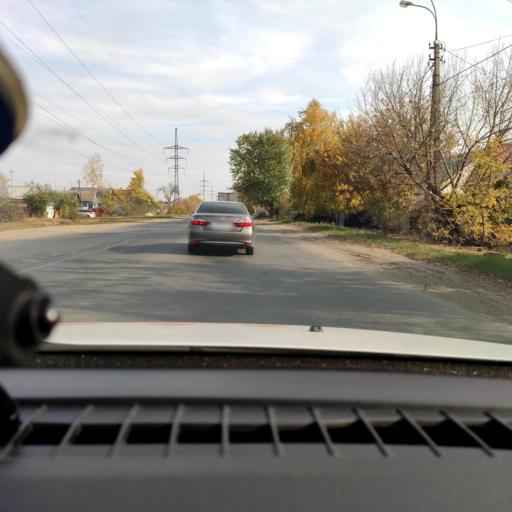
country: RU
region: Samara
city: Samara
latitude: 53.1336
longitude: 50.1247
